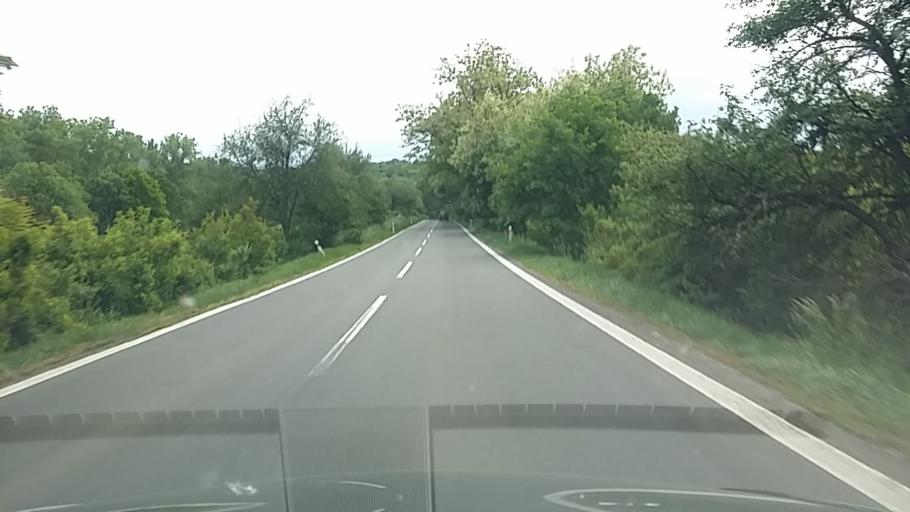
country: SK
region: Banskobystricky
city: Krupina
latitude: 48.2965
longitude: 19.0212
